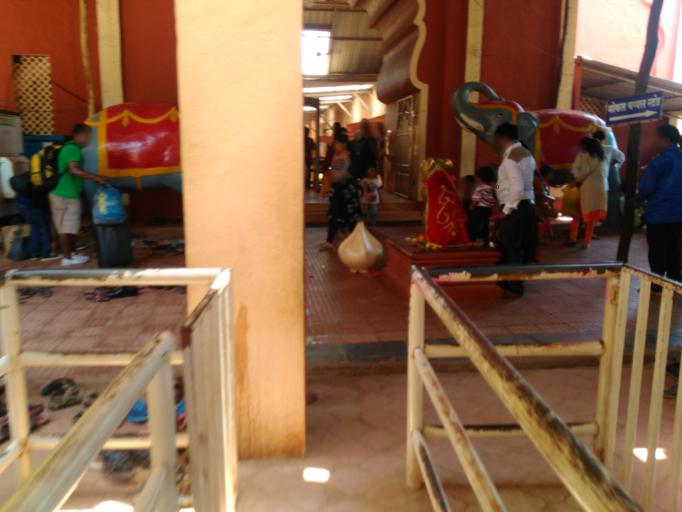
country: IN
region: Maharashtra
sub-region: Ratnagiri
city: Ratnagiri
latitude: 17.1456
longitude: 73.2664
